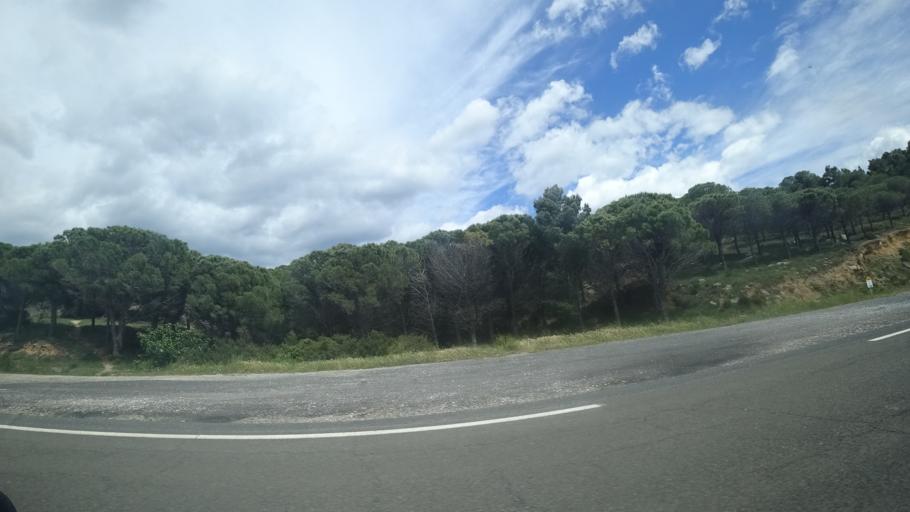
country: FR
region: Languedoc-Roussillon
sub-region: Departement de l'Aude
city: Leucate
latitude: 42.9150
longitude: 3.0213
